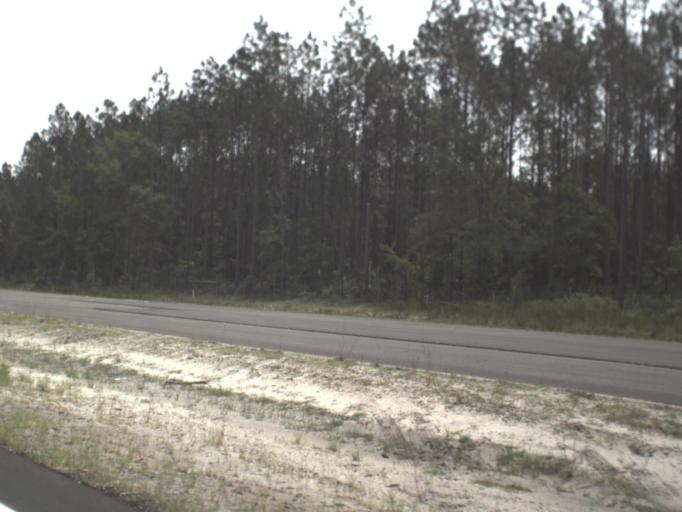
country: US
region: Florida
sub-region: Duval County
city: Baldwin
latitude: 30.4241
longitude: -81.9260
